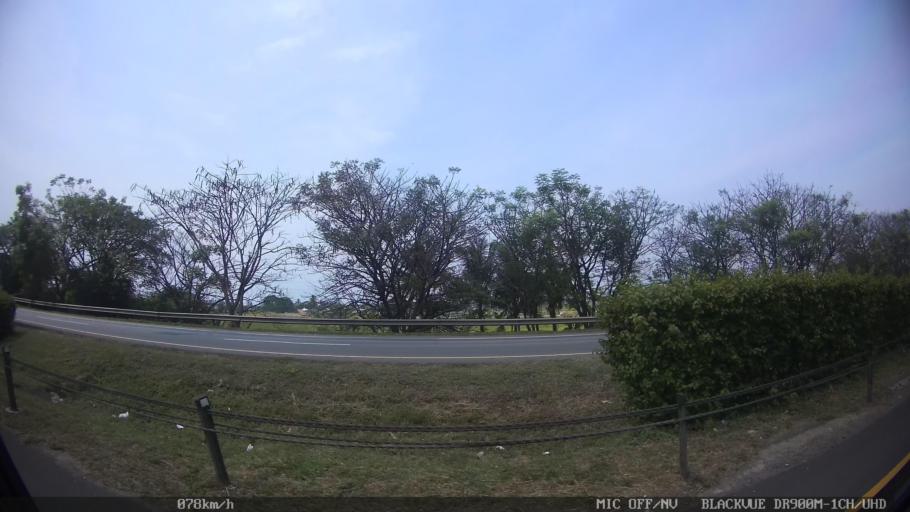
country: ID
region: Banten
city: Bojonegara
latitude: -6.0302
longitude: 106.0989
